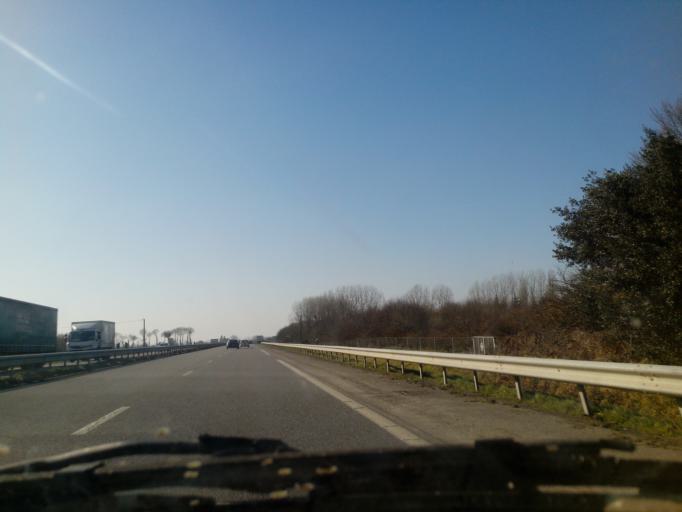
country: FR
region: Brittany
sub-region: Departement des Cotes-d'Armor
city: Saint-Barnabe
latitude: 48.1801
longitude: -2.7001
